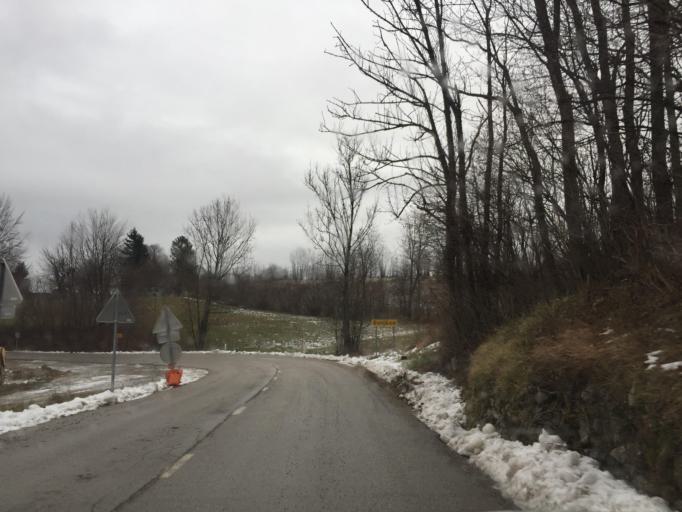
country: SI
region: Kanal
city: Kanal
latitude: 46.0550
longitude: 13.6850
